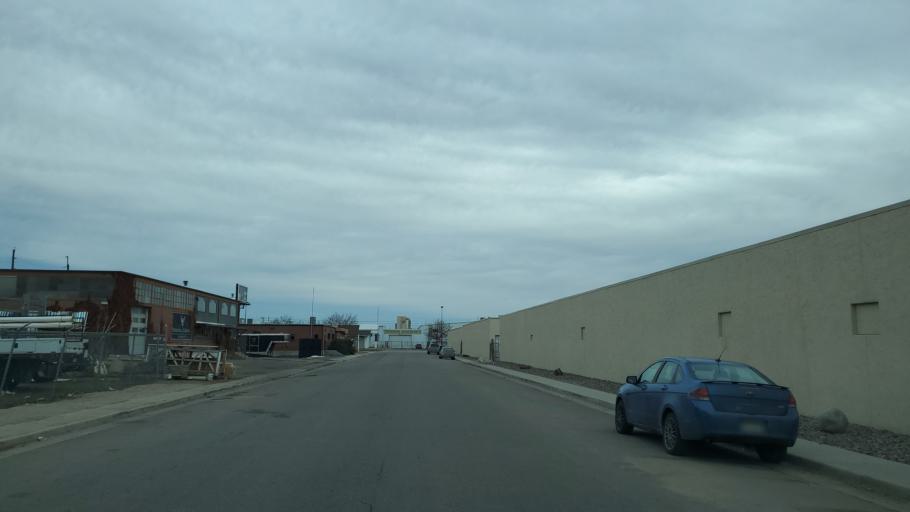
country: US
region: Colorado
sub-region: Denver County
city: Denver
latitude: 39.6952
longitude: -104.9980
